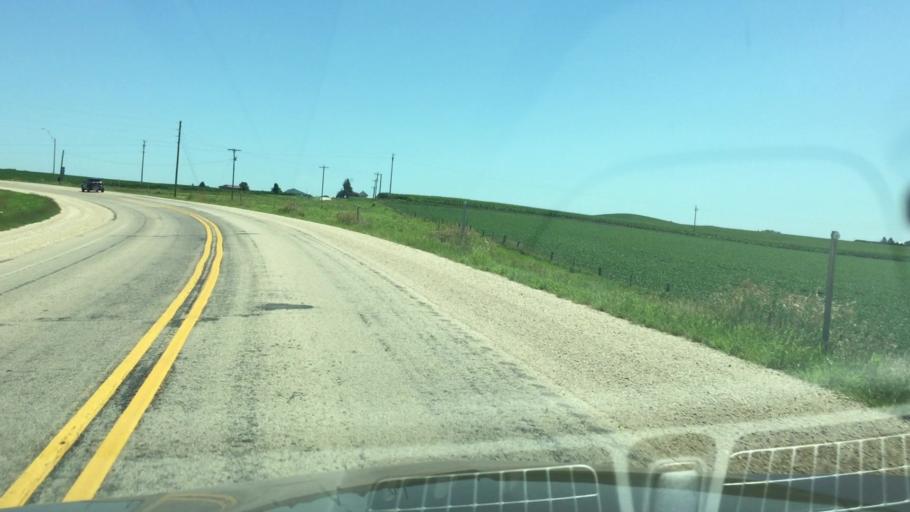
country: US
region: Iowa
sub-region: Cedar County
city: Mechanicsville
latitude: 41.9615
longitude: -91.1454
